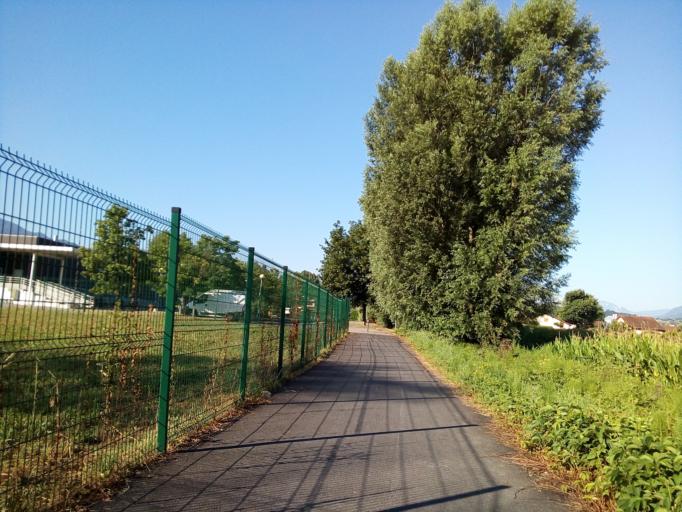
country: FR
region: Rhone-Alpes
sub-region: Departement de l'Isere
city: Crolles
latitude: 45.2766
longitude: 5.8966
